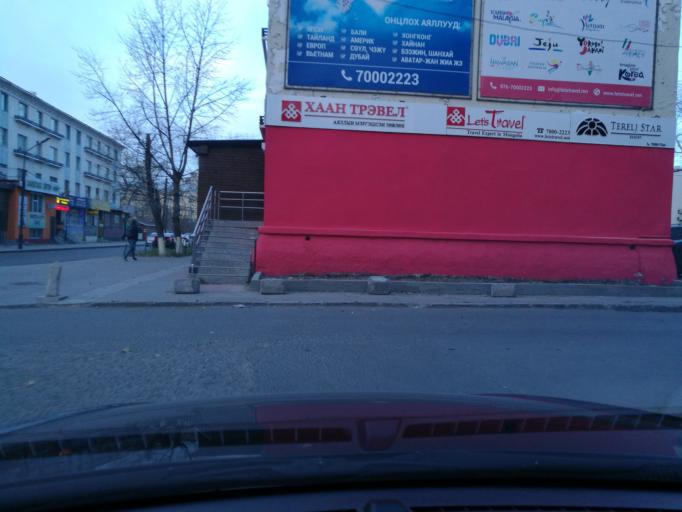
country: MN
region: Ulaanbaatar
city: Ulaanbaatar
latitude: 47.9246
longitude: 106.9201
